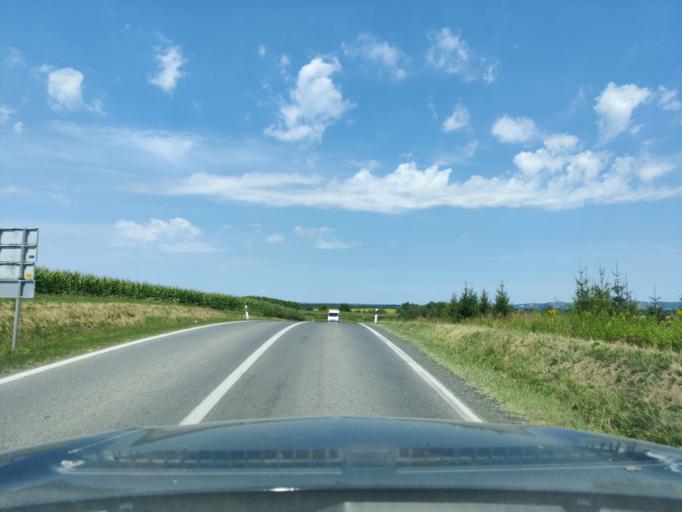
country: HR
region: Medimurska
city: Vratisinec
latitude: 46.4782
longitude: 16.4238
